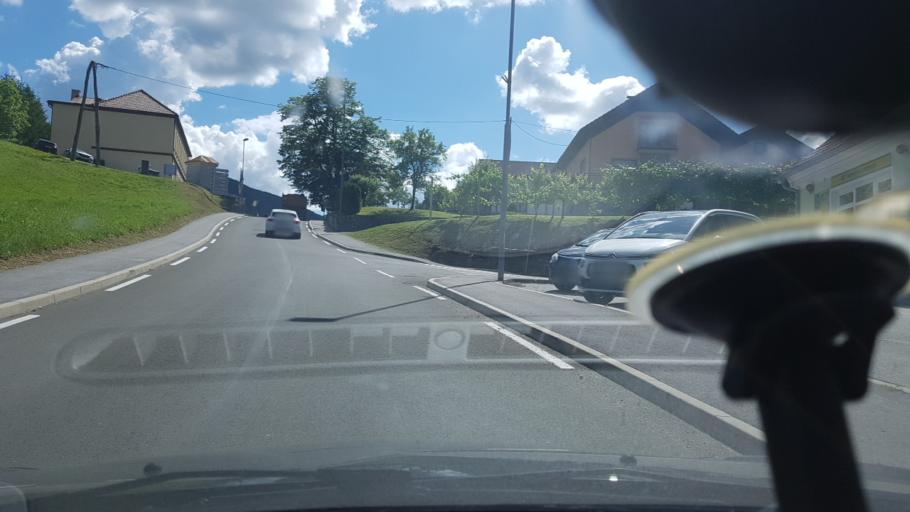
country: SI
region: Zetale
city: Zetale
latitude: 46.2750
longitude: 15.7921
